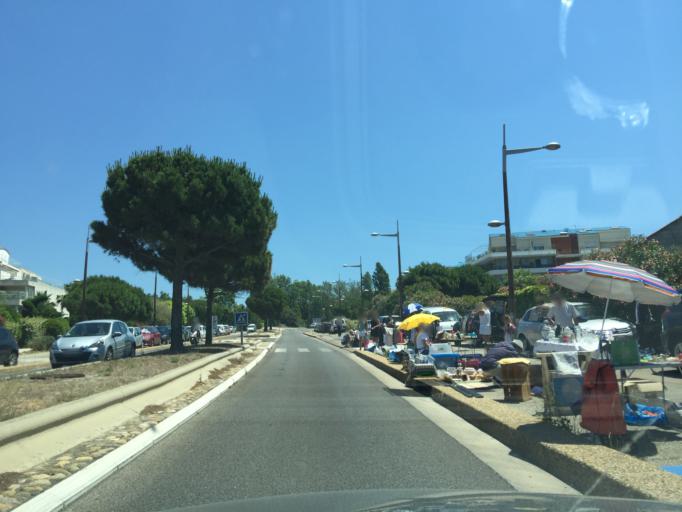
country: FR
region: Provence-Alpes-Cote d'Azur
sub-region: Departement des Bouches-du-Rhone
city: Marseille 08
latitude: 43.2446
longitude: 5.3778
